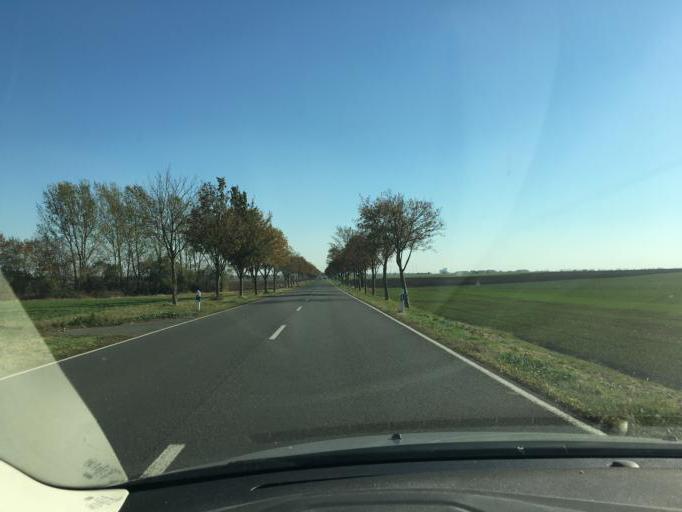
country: DE
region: Saxony-Anhalt
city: Wanzleben
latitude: 52.0276
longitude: 11.4860
